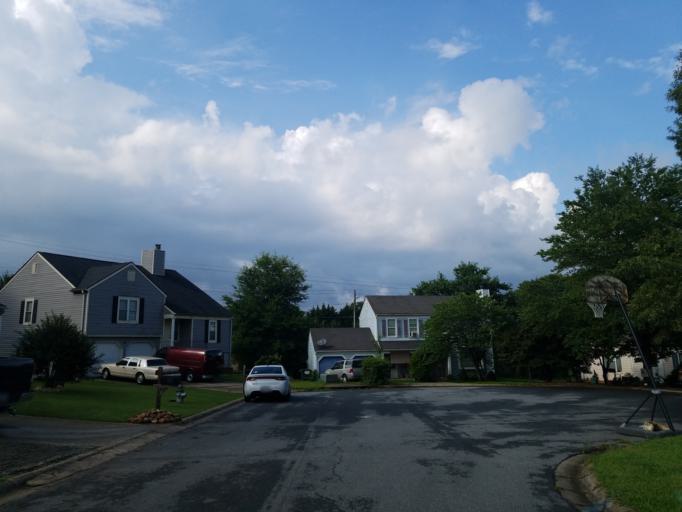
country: US
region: Georgia
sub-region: Cobb County
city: Marietta
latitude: 33.9930
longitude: -84.5486
